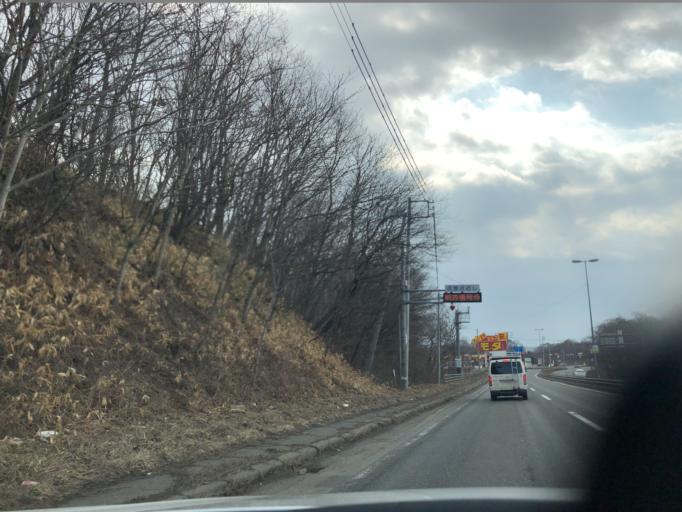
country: JP
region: Hokkaido
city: Chitose
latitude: 42.7695
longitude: 141.7083
